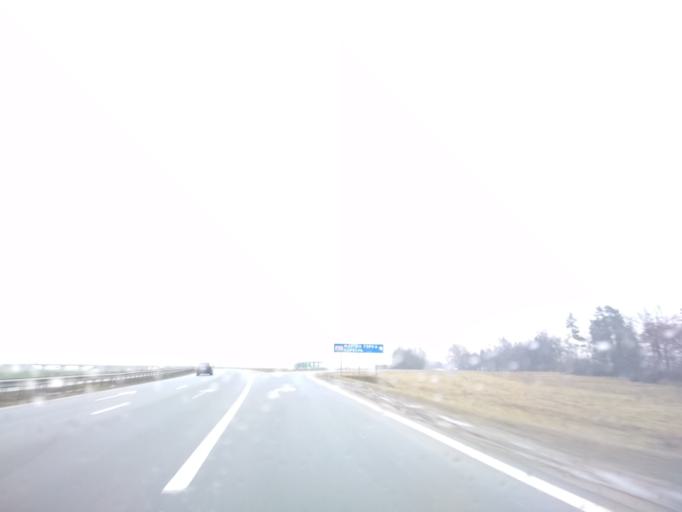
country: BY
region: Minsk
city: Blon'
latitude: 53.5492
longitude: 28.1626
